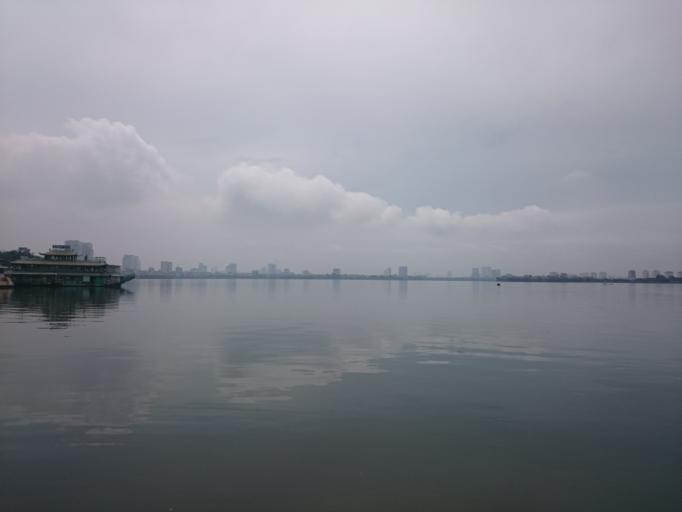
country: VN
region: Ha Noi
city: Hanoi
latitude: 21.0449
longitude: 105.8361
